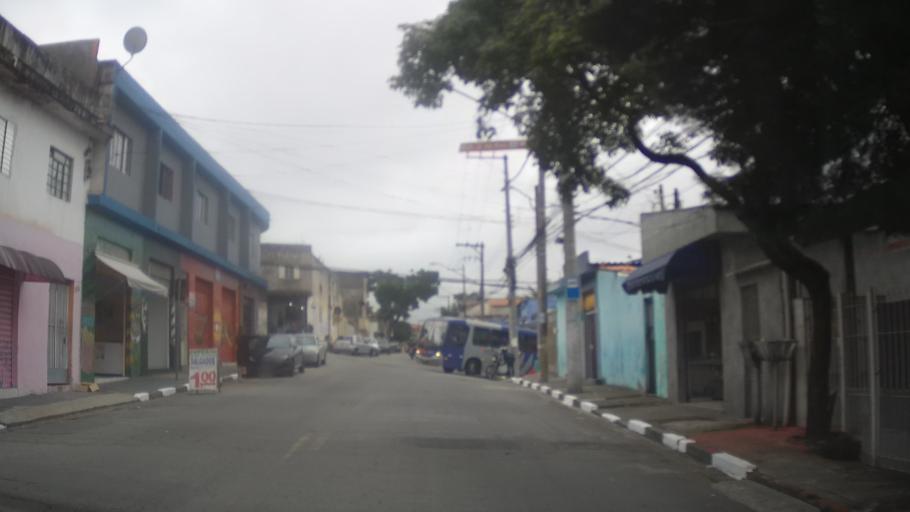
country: BR
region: Sao Paulo
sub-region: Guarulhos
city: Guarulhos
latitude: -23.4416
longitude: -46.5160
